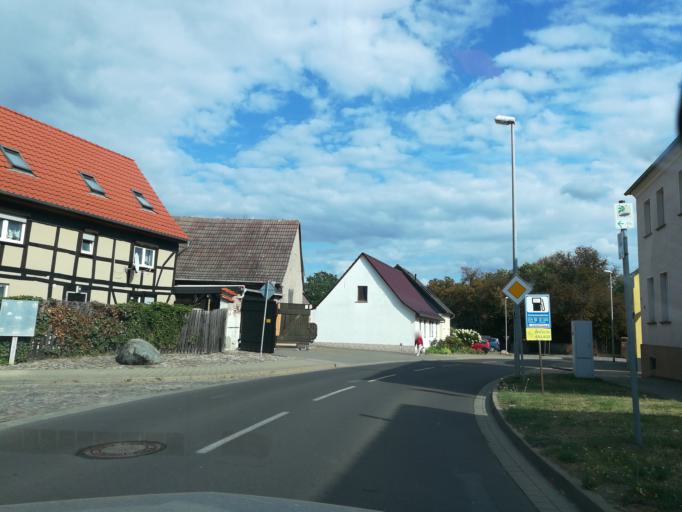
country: DE
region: Saxony-Anhalt
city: Niederndodeleben
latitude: 52.1400
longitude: 11.4978
